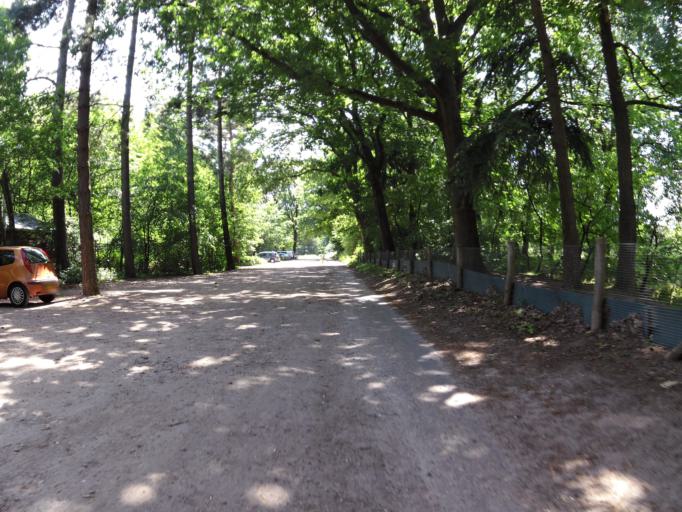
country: NL
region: North Brabant
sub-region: Gemeente Son en Breugel
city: Son
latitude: 51.5147
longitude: 5.4655
